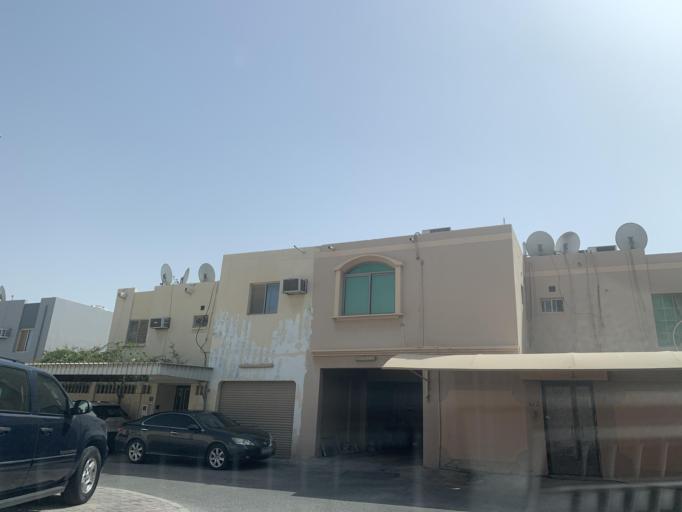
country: BH
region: Northern
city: Ar Rifa'
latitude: 26.1414
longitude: 50.5690
